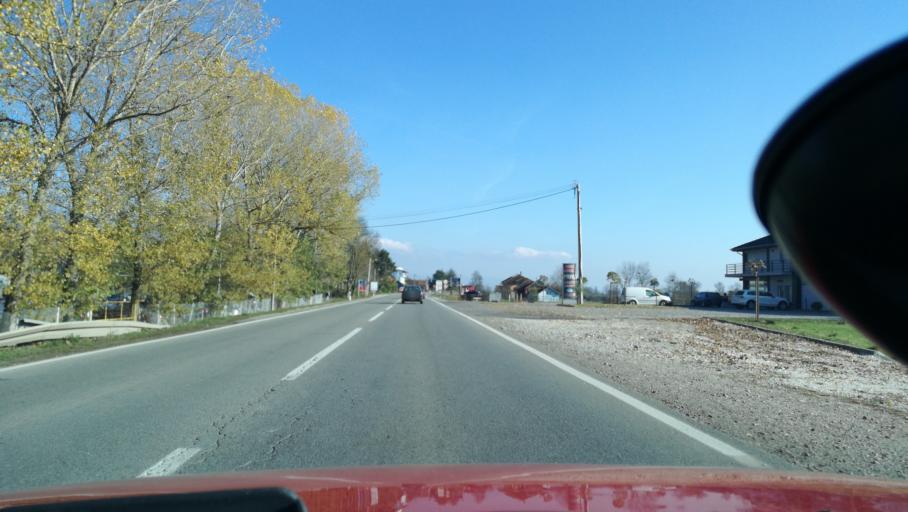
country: RS
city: Prislonica
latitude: 43.8878
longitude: 20.4606
